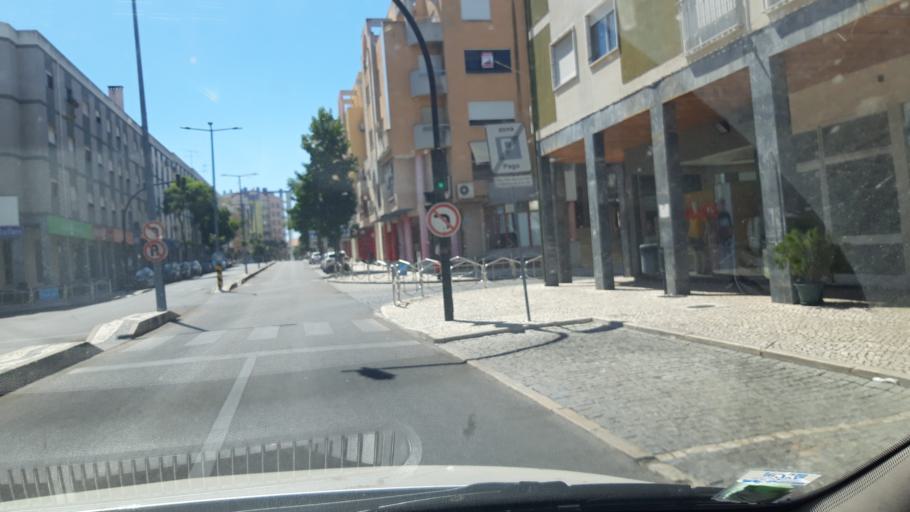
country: PT
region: Santarem
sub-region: Entroncamento
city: Entroncamento
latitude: 39.4611
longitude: -8.4692
